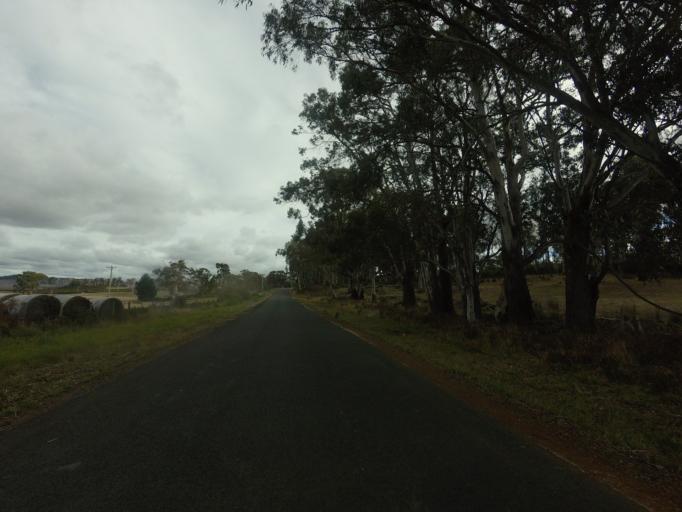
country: AU
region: Tasmania
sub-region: Brighton
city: Bridgewater
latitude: -42.3980
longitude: 147.3851
